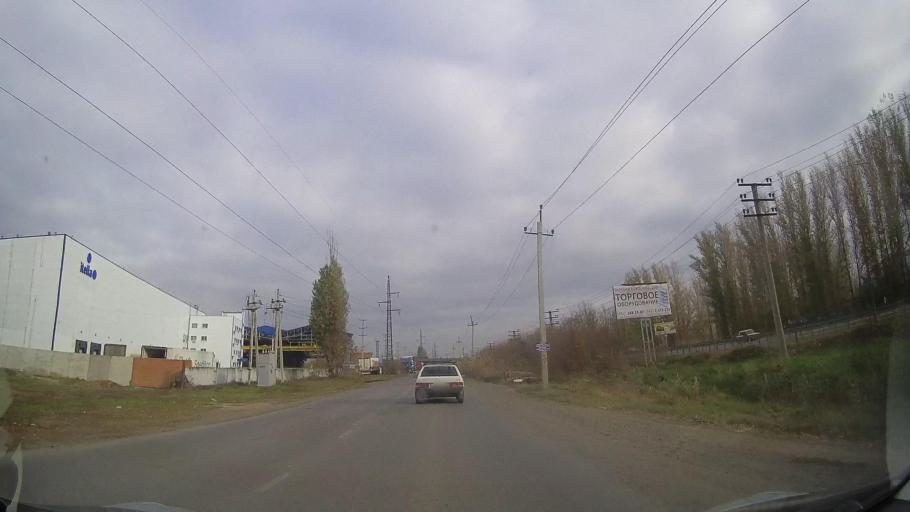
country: RU
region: Rostov
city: Bataysk
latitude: 47.1121
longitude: 39.7661
